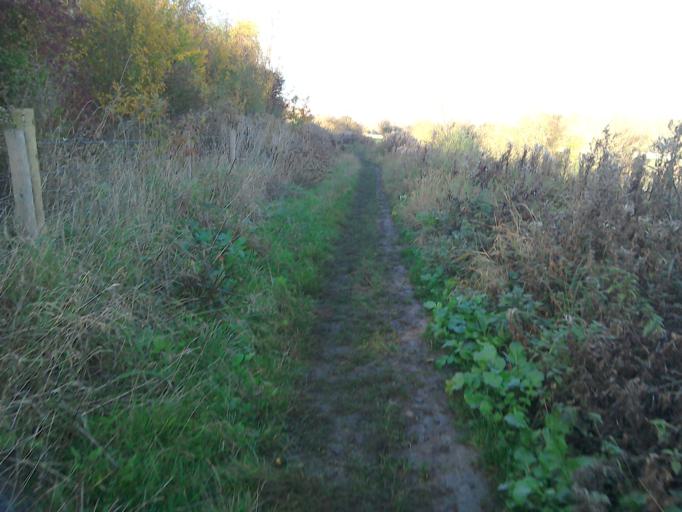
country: GB
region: England
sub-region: Oxfordshire
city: Radley
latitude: 51.7012
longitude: -1.2320
